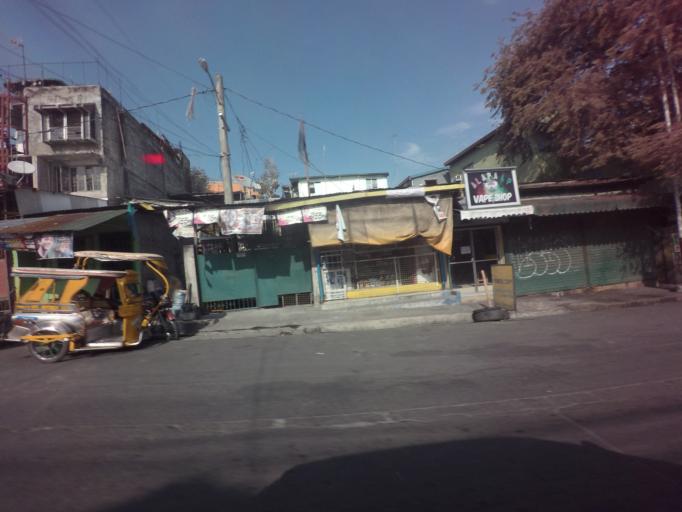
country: PH
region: Calabarzon
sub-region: Province of Rizal
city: Taguig
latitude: 14.4997
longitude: 121.0498
